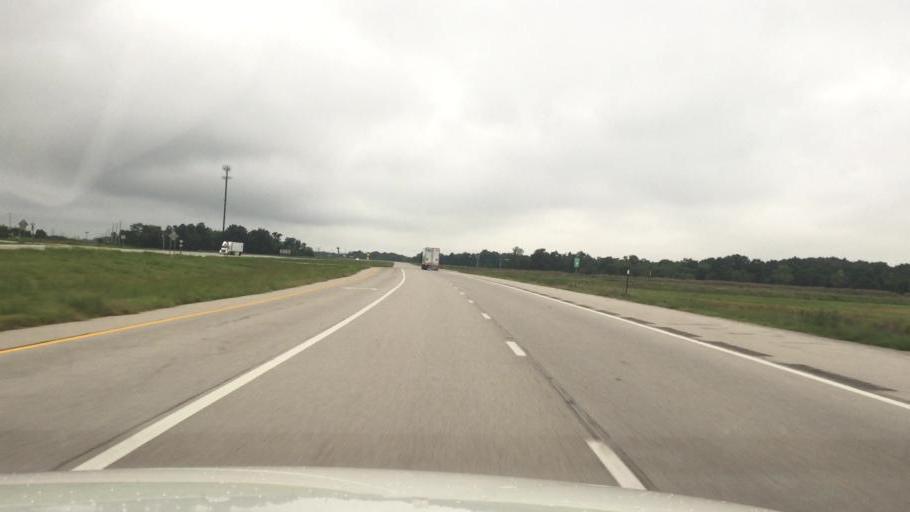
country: US
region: Kansas
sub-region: Montgomery County
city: Coffeyville
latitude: 37.1097
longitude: -95.5861
